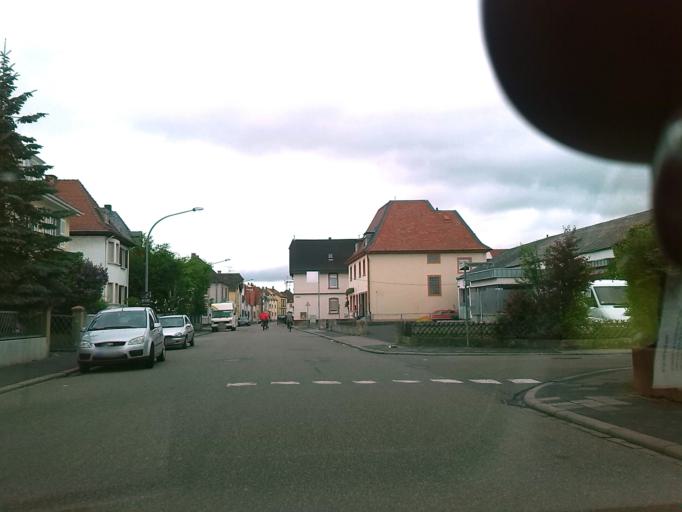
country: DE
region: Rheinland-Pfalz
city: Hassloch
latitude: 49.3676
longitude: 8.2549
